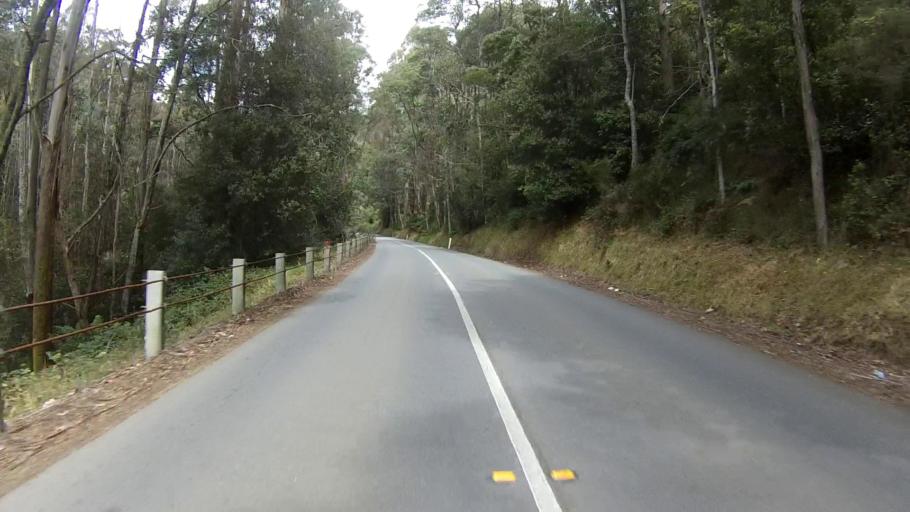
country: AU
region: Tasmania
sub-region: Kingborough
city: Kettering
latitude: -43.1262
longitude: 147.1794
